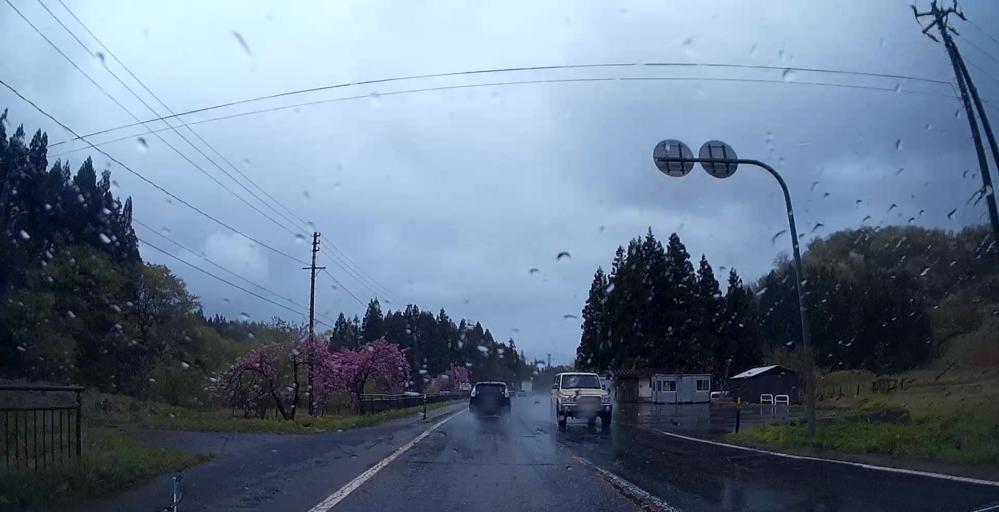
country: JP
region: Niigata
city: Murakami
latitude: 38.0729
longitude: 139.7316
